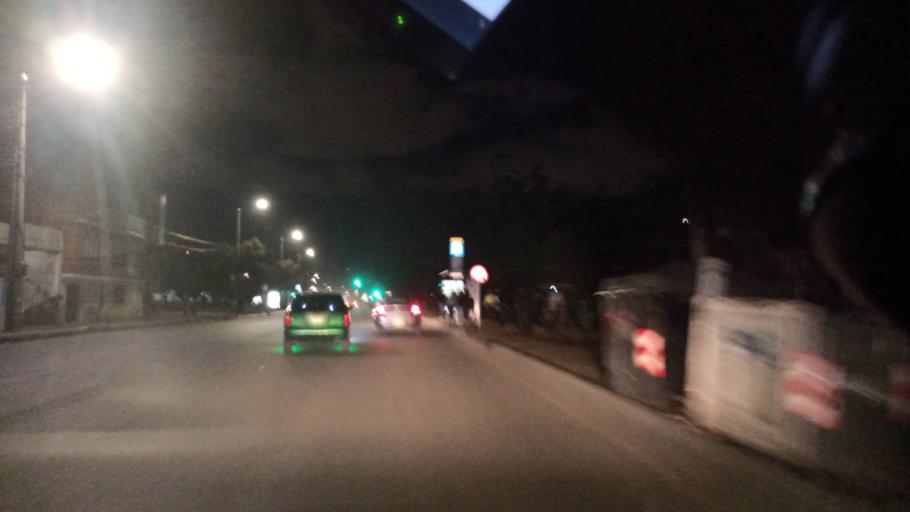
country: CO
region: Cundinamarca
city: Funza
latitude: 4.6810
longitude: -74.1535
